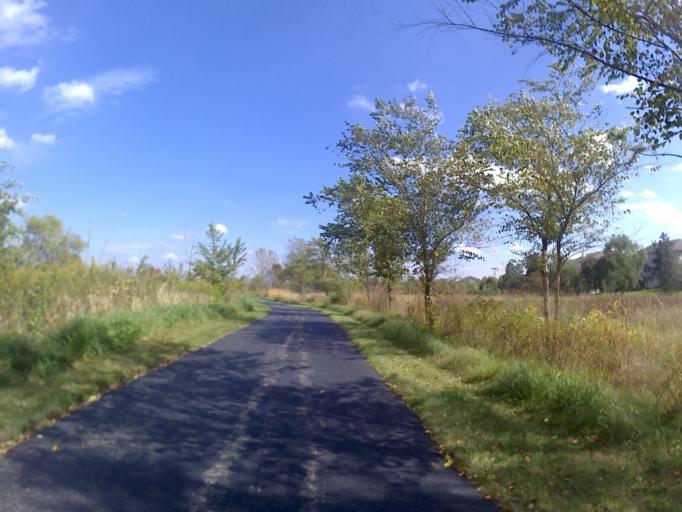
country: US
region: Illinois
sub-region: Will County
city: Bolingbrook
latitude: 41.7101
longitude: -88.1060
